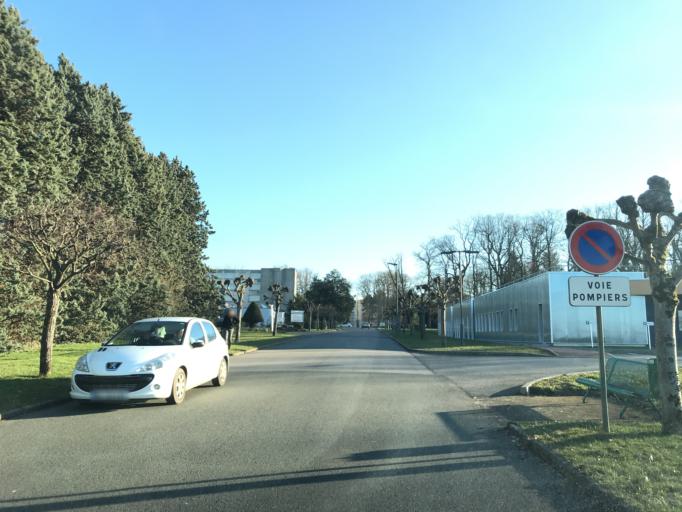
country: FR
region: Haute-Normandie
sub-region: Departement de l'Eure
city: Saint-Sebastien-de-Morsent
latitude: 49.0044
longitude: 1.0774
